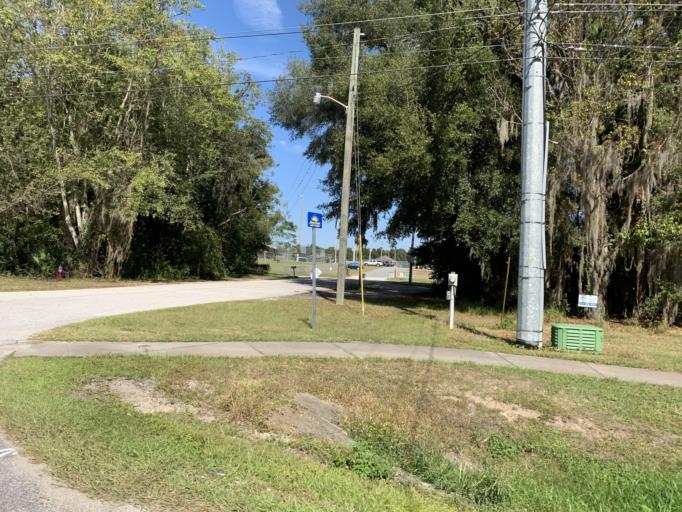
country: US
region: Florida
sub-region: Marion County
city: Ocala
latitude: 29.1639
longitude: -82.0730
